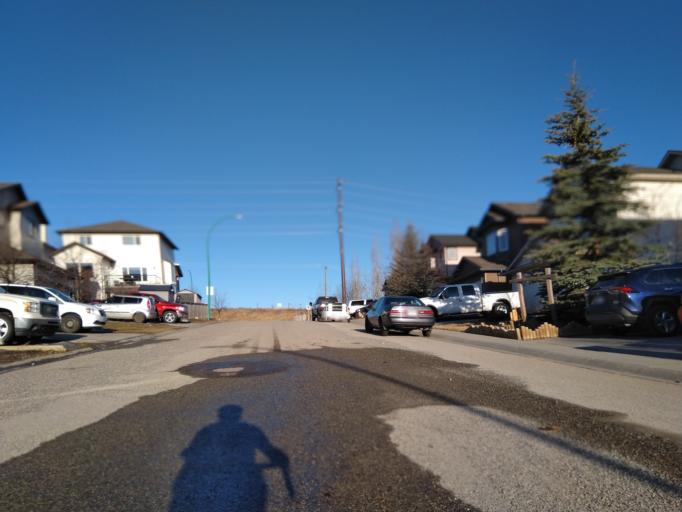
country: CA
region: Alberta
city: Cochrane
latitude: 51.1862
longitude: -114.5121
